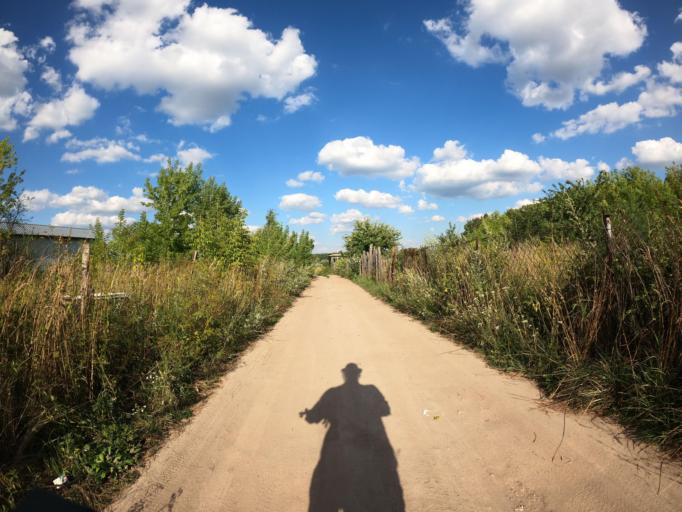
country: RU
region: Moskovskaya
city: Peski
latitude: 55.1931
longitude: 38.7452
